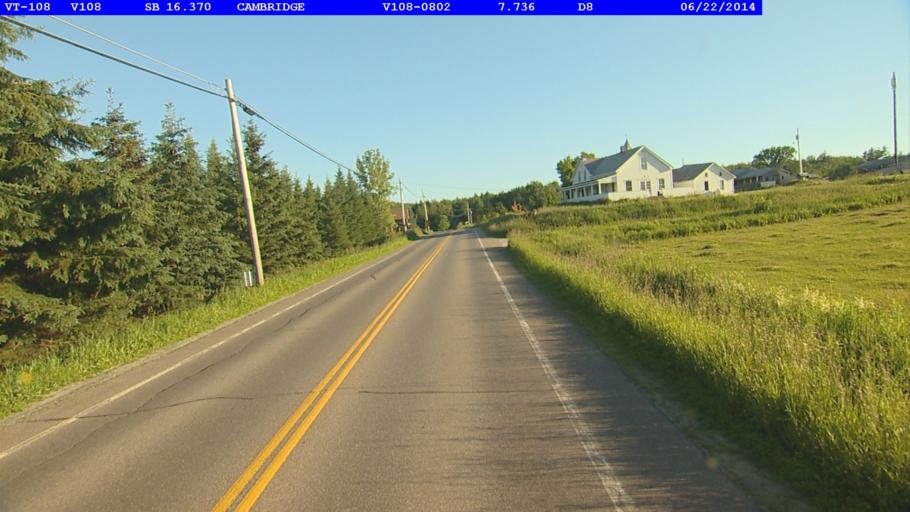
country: US
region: Vermont
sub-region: Lamoille County
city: Johnson
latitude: 44.6302
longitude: -72.8302
